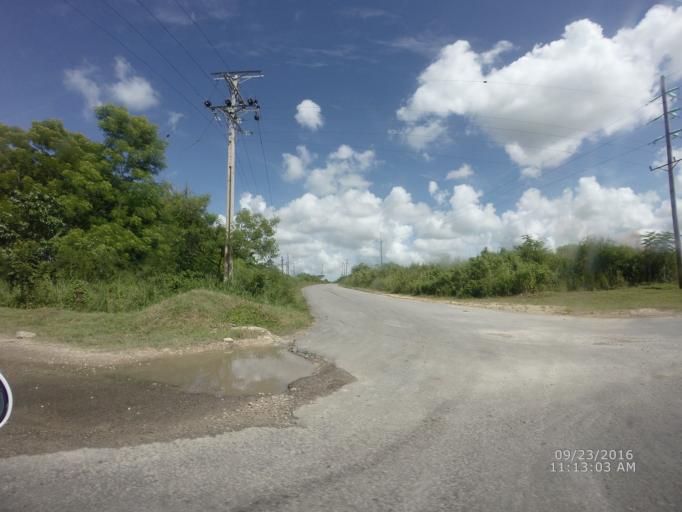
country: CU
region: La Habana
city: Arroyo Naranjo
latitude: 23.0303
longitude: -82.2923
